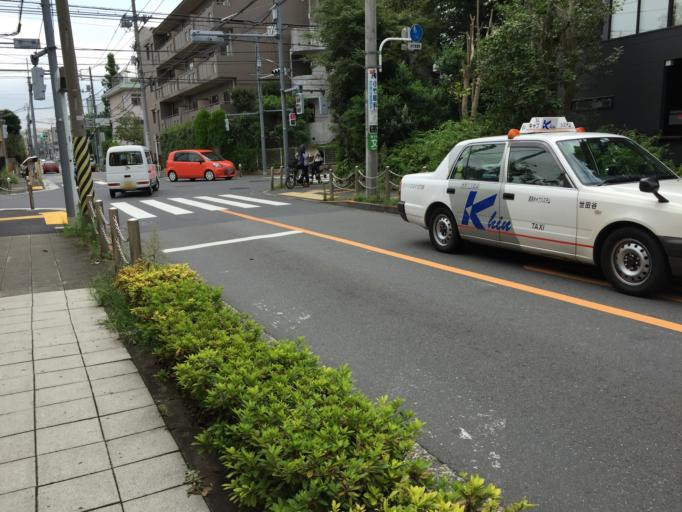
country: JP
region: Tokyo
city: Tokyo
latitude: 35.6573
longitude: 139.6381
